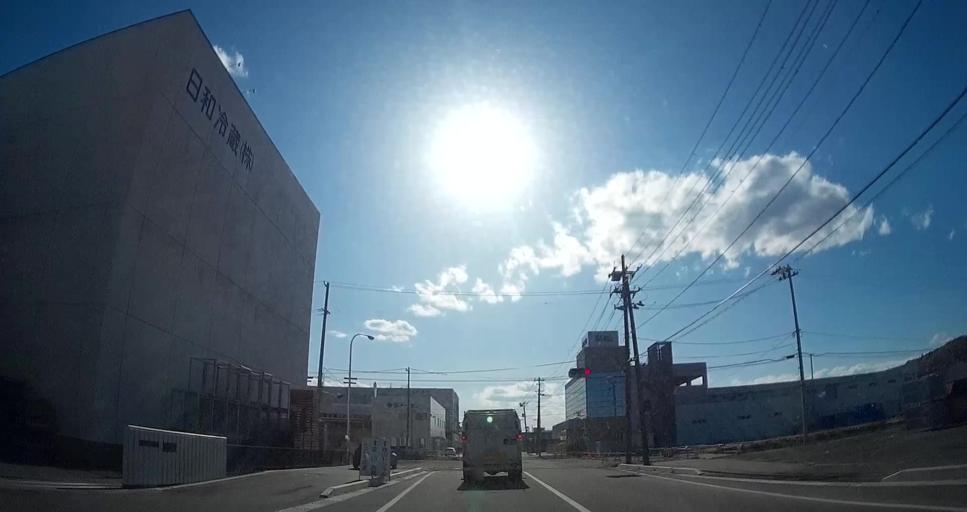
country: JP
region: Miyagi
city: Ishinomaki
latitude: 38.4147
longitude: 141.3361
